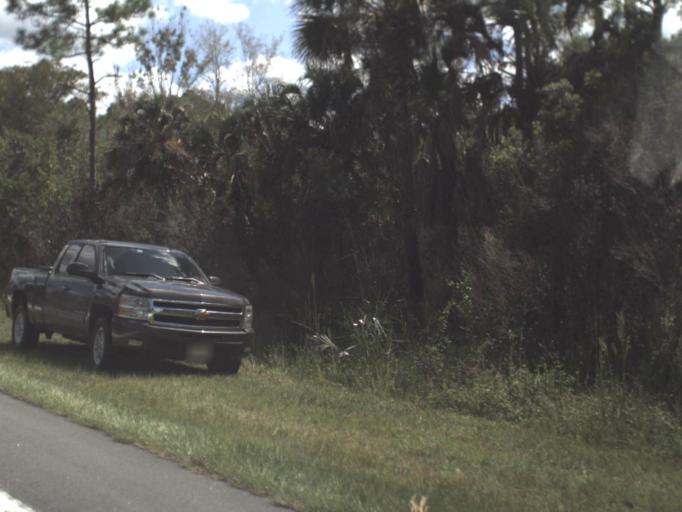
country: US
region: Florida
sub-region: Collier County
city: Marco
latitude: 25.8831
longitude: -81.2518
